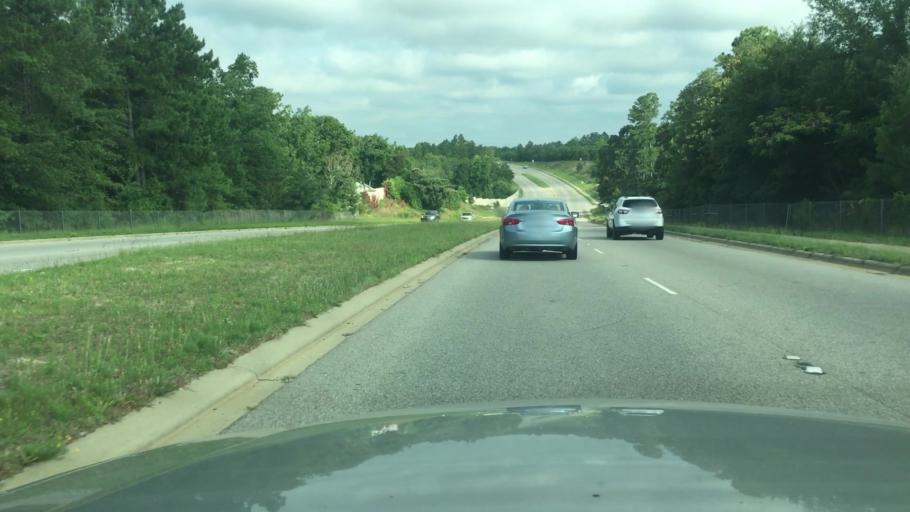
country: US
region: North Carolina
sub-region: Cumberland County
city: Hope Mills
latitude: 34.9847
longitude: -78.9322
